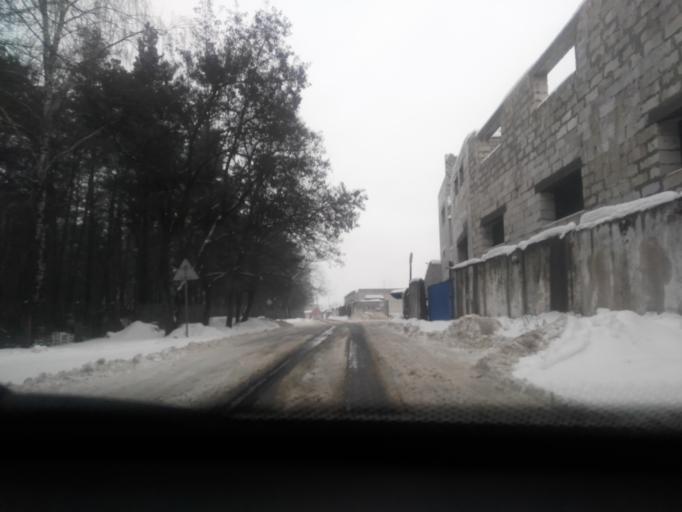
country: BY
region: Mogilev
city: Babruysk
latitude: 53.1685
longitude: 29.2090
